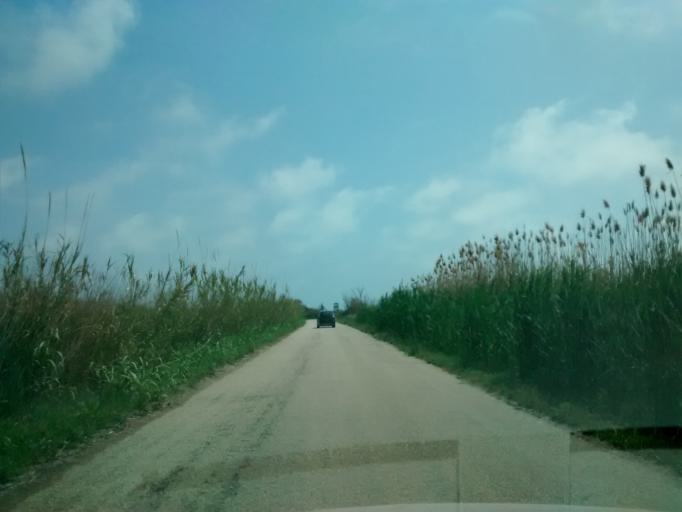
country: ES
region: Catalonia
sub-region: Provincia de Tarragona
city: Deltebre
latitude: 40.6908
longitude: 0.8439
